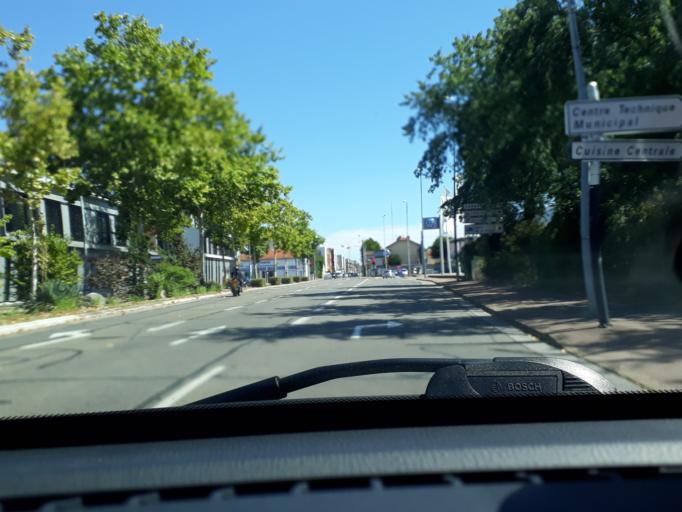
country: FR
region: Rhone-Alpes
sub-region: Departement du Rhone
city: Saint-Priest
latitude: 45.6972
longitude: 4.9247
